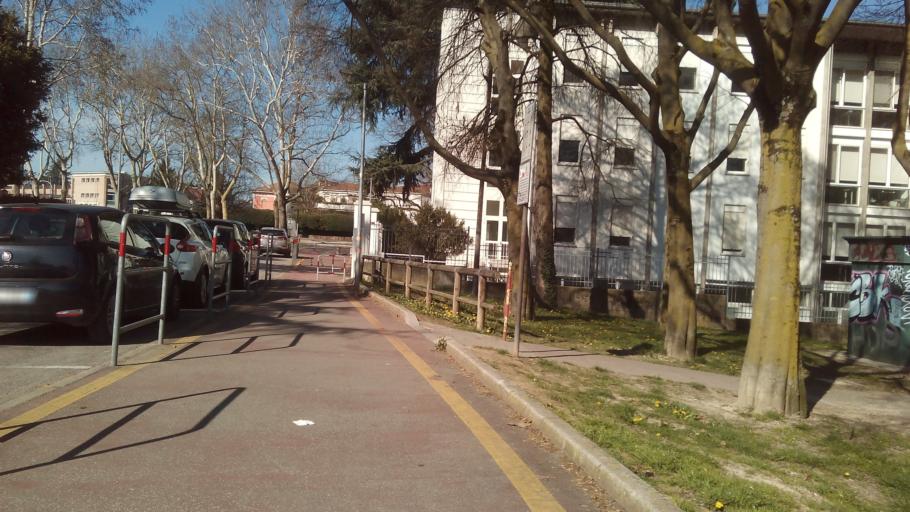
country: IT
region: Lombardy
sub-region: Provincia di Mantova
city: Mantova
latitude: 45.1563
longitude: 10.7716
